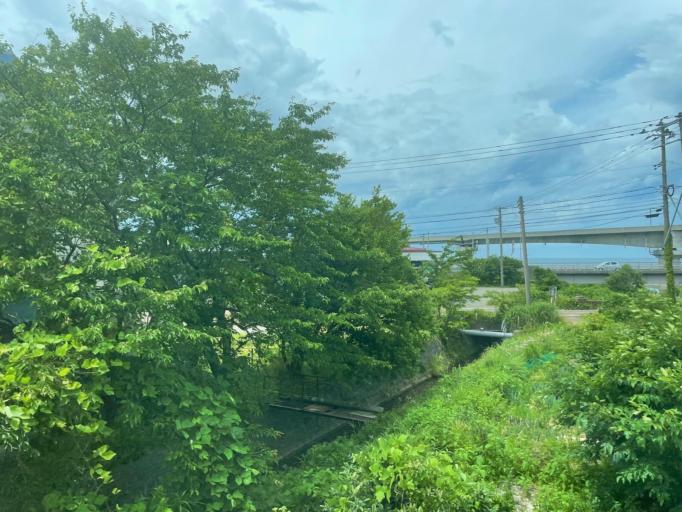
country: JP
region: Niigata
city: Itoigawa
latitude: 37.0498
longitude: 137.8841
